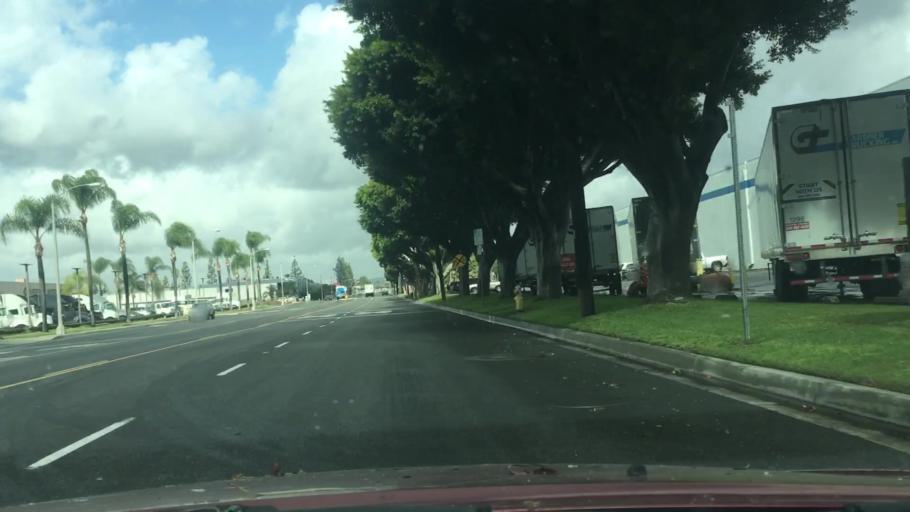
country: US
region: California
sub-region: Los Angeles County
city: La Mirada
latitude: 33.8897
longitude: -118.0289
